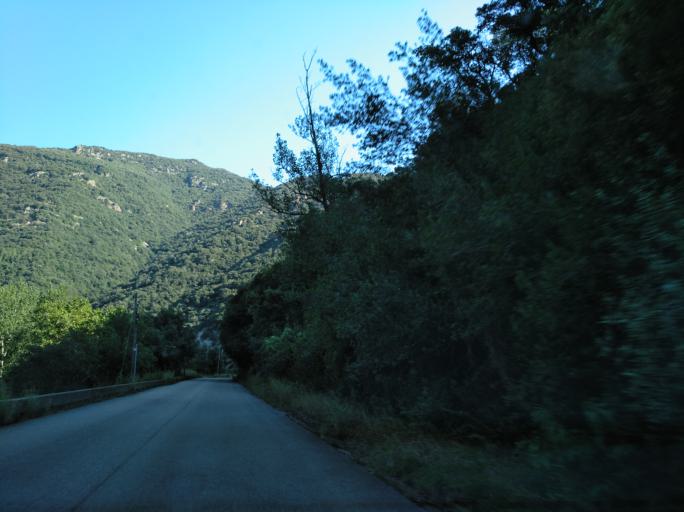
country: ES
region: Catalonia
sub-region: Provincia de Girona
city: Susqueda
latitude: 41.9890
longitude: 2.5703
